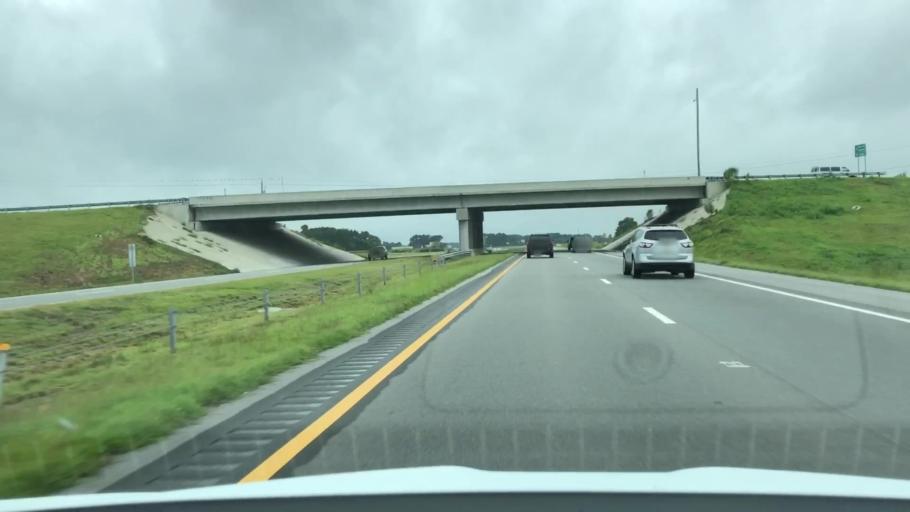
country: US
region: North Carolina
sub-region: Wayne County
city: Elroy
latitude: 35.4117
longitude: -77.8964
